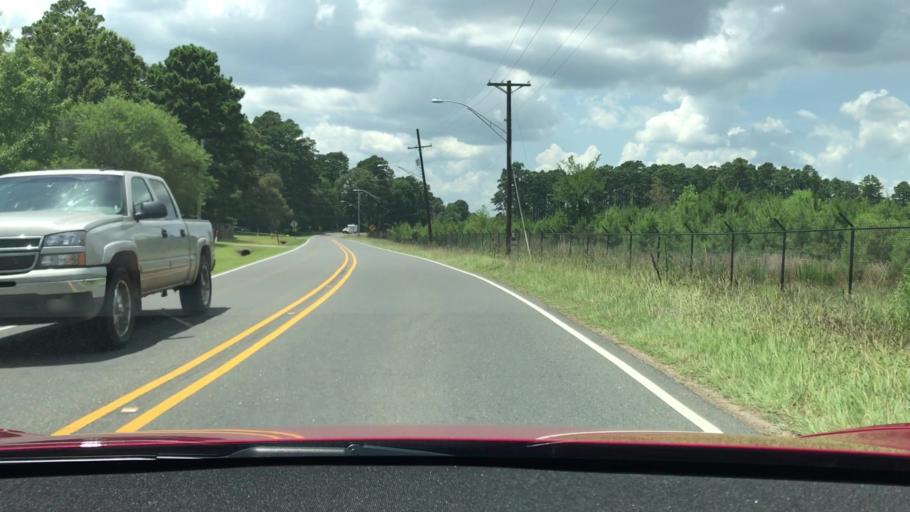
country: US
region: Louisiana
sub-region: Bossier Parish
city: Bossier City
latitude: 32.3841
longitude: -93.7142
